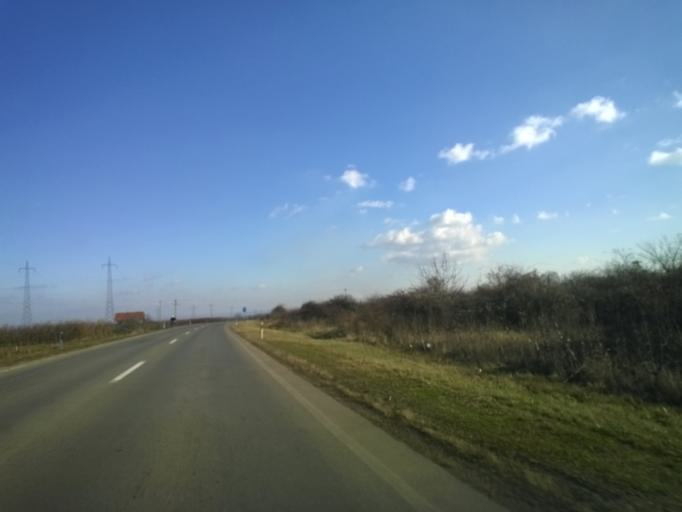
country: RS
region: Central Serbia
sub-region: Podunavski Okrug
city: Smederevo
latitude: 44.6122
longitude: 20.9221
